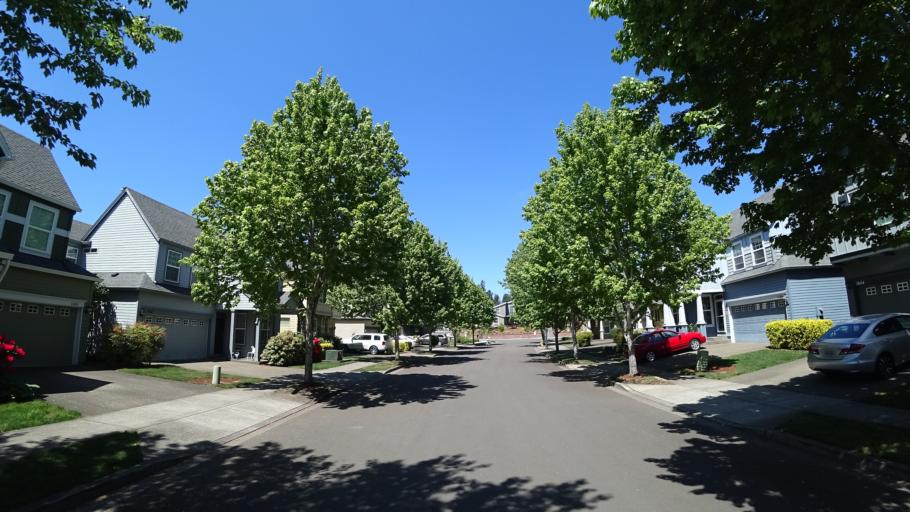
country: US
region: Oregon
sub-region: Washington County
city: Hillsboro
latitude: 45.5091
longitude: -122.9770
